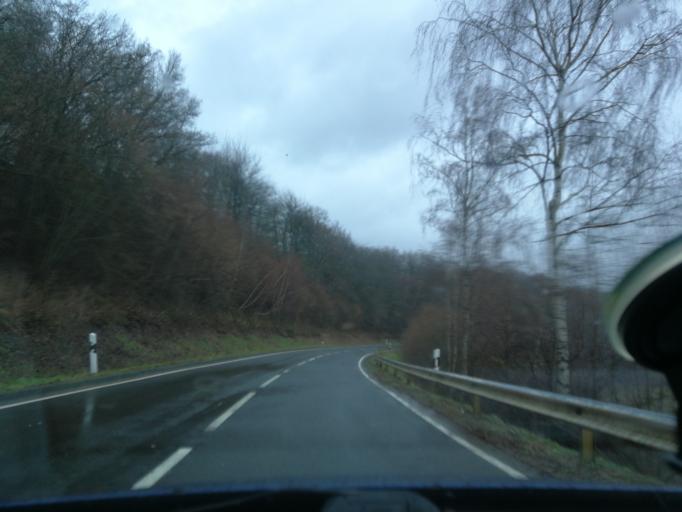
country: DE
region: Rheinland-Pfalz
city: Deuselbach
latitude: 49.7557
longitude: 7.0502
